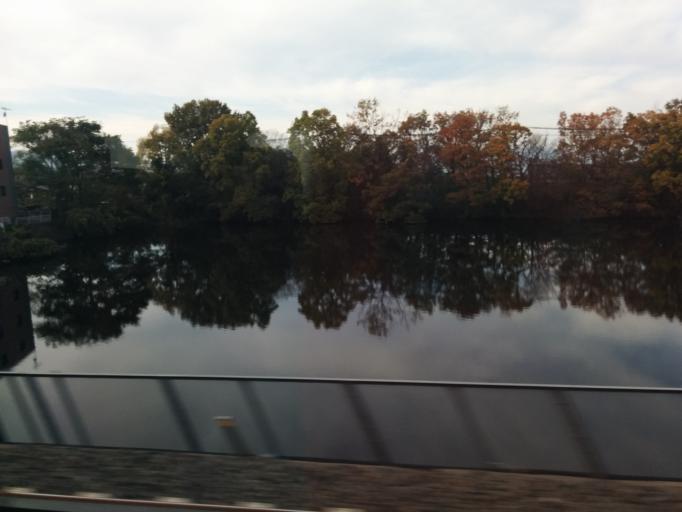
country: JP
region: Shiga Prefecture
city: Kusatsu
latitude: 34.9746
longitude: 135.9321
